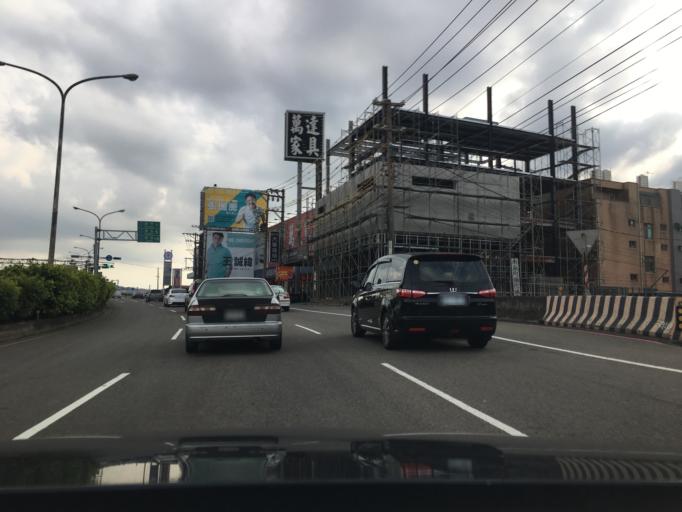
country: TW
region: Taiwan
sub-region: Hsinchu
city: Zhubei
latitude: 24.8269
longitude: 120.9978
